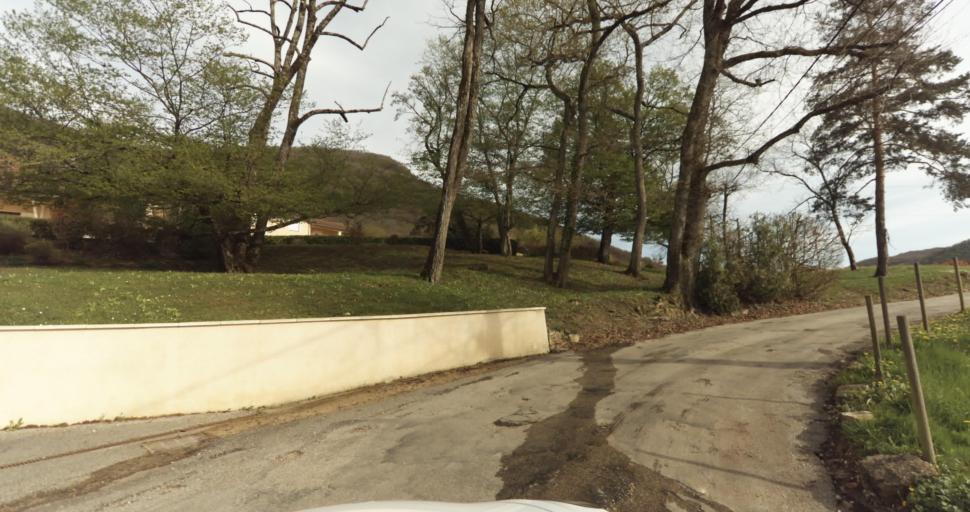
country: FR
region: Rhone-Alpes
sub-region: Departement de l'Ain
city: Vaux-en-Bugey
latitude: 45.9406
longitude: 5.3802
